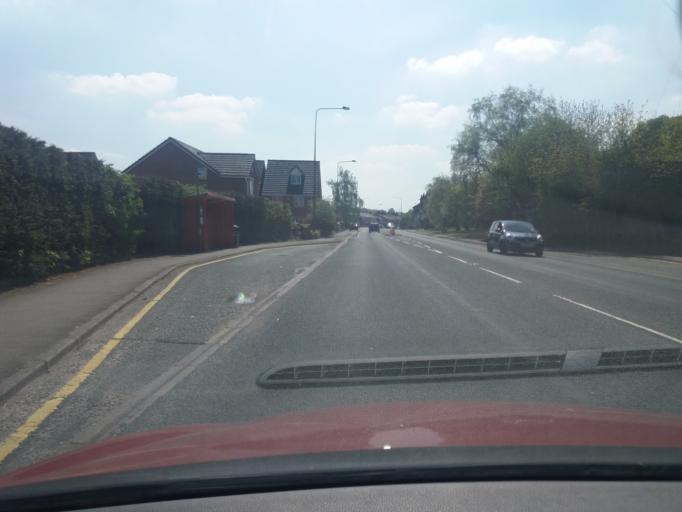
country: GB
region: England
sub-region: Lancashire
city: Clayton-le-Woods
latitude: 53.6964
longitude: -2.6387
